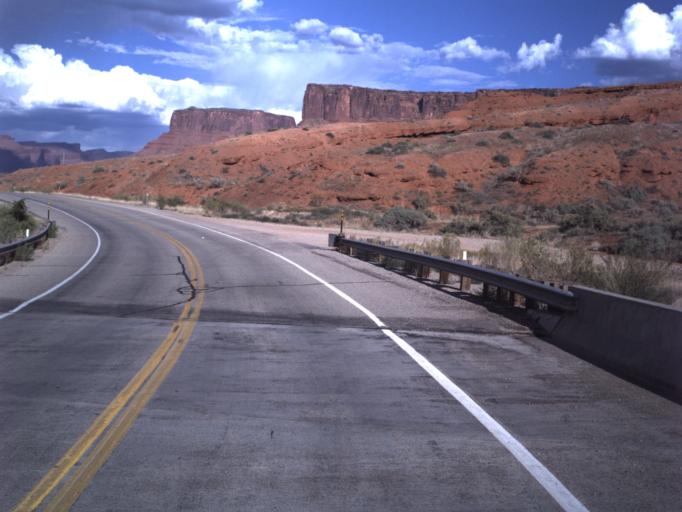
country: US
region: Utah
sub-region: Grand County
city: Moab
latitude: 38.6776
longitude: -109.4493
